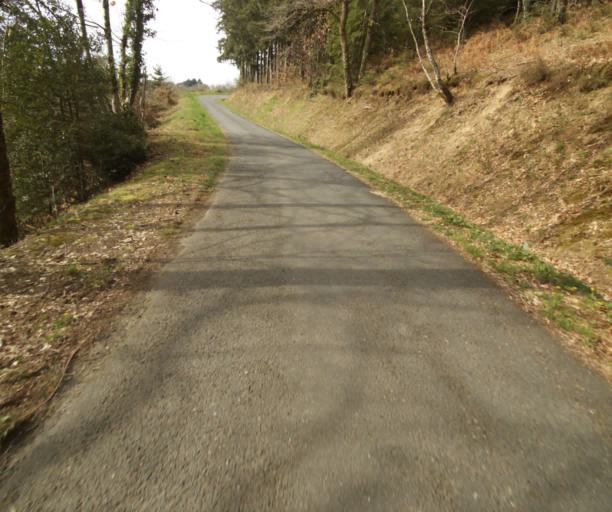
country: FR
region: Limousin
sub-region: Departement de la Correze
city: Correze
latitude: 45.4160
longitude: 1.8098
